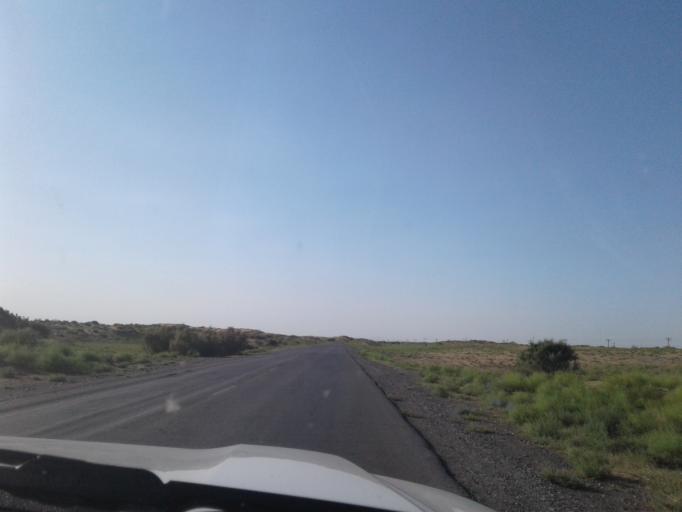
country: TM
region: Mary
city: Yoloeten
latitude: 37.1475
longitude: 62.4376
